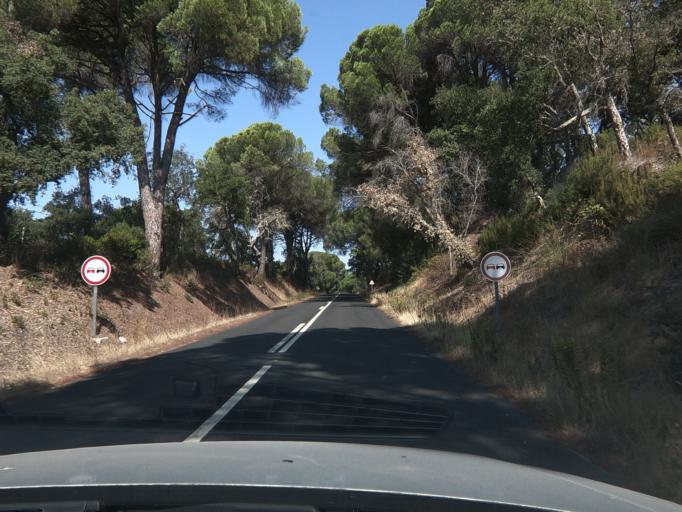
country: PT
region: Setubal
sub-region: Alcacer do Sal
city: Alcacer do Sal
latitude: 38.3219
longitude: -8.4392
